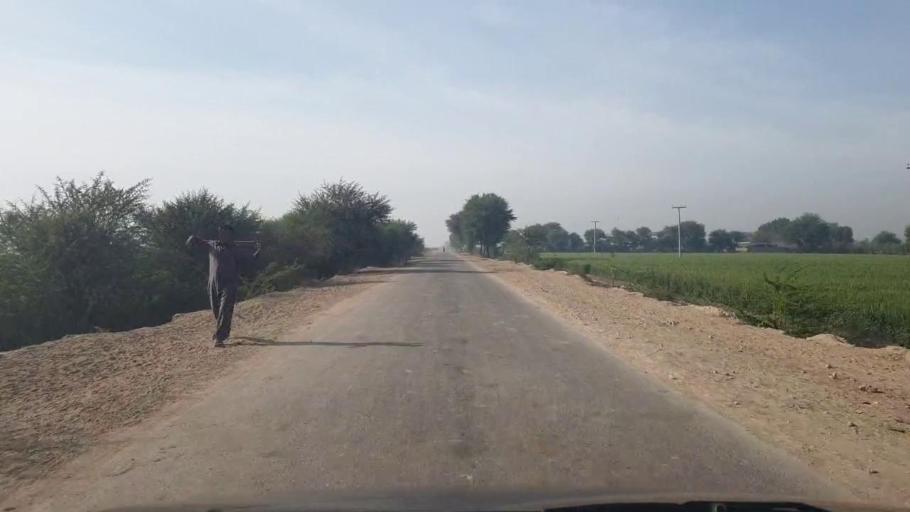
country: PK
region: Sindh
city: Umarkot
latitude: 25.3640
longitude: 69.7034
